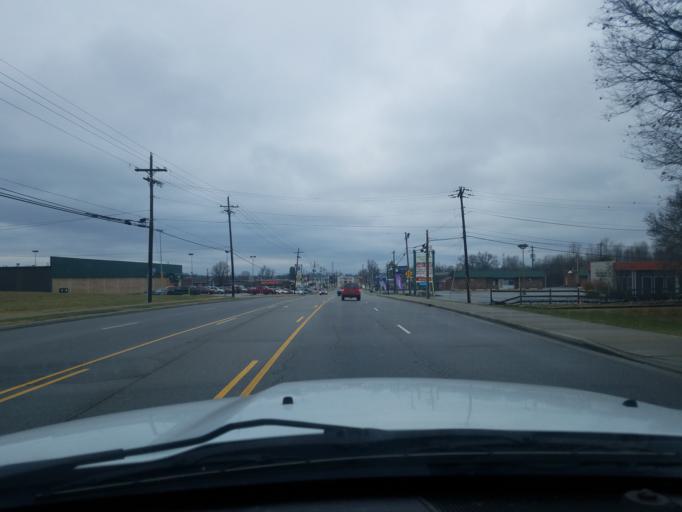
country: US
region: Indiana
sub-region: Floyd County
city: New Albany
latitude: 38.3301
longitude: -85.8187
